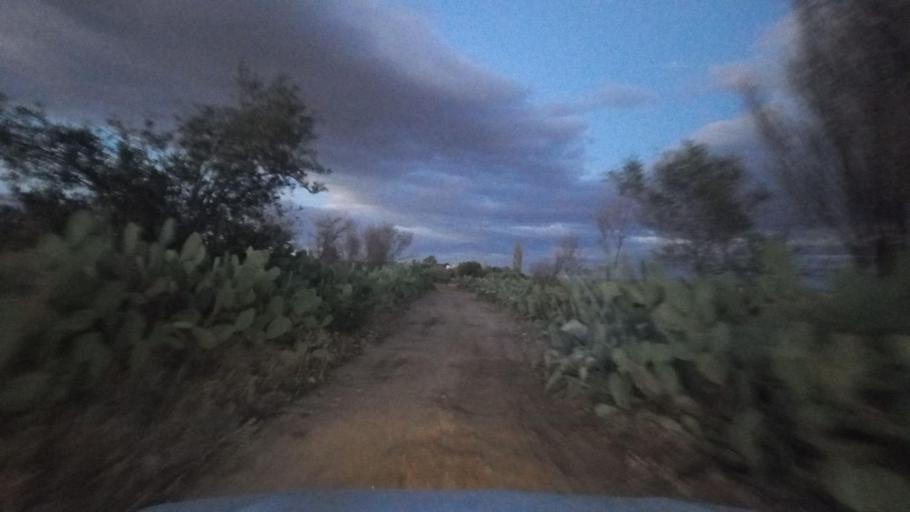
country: TN
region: Al Qasrayn
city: Kasserine
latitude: 35.2542
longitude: 8.9371
